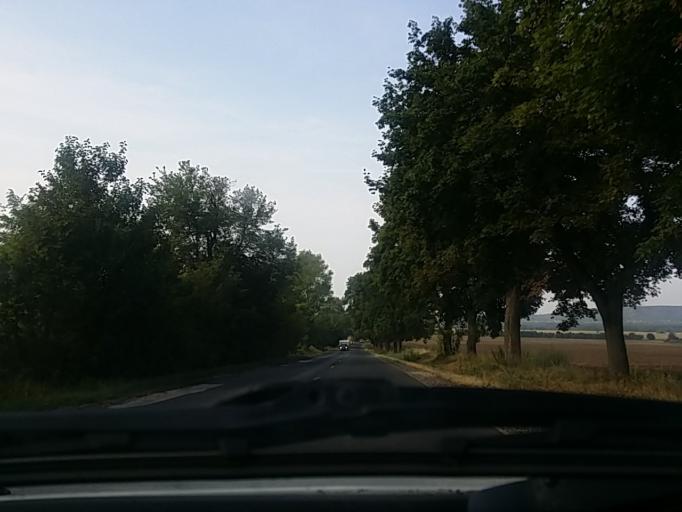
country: HU
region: Fejer
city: Csakvar
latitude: 47.4183
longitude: 18.5025
